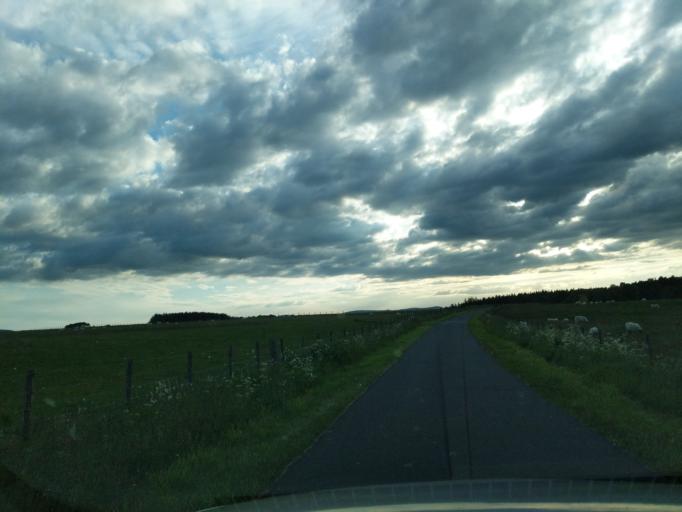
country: GB
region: Scotland
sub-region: Midlothian
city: Penicuik
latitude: 55.7645
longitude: -3.1344
